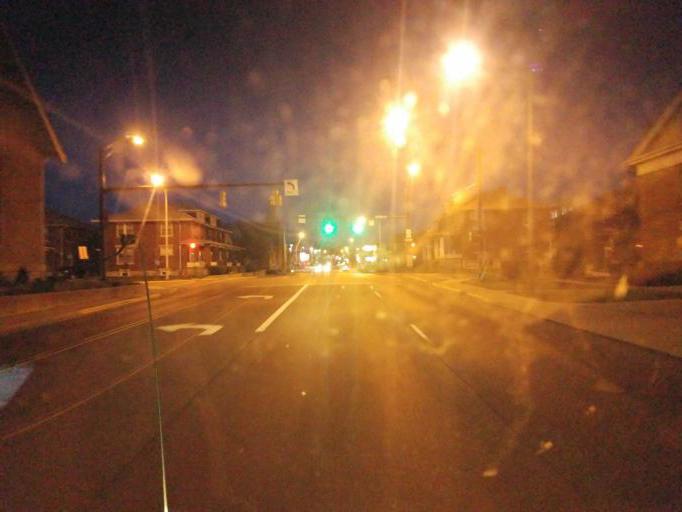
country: US
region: Ohio
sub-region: Logan County
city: Bellefontaine
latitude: 40.3628
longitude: -83.7620
